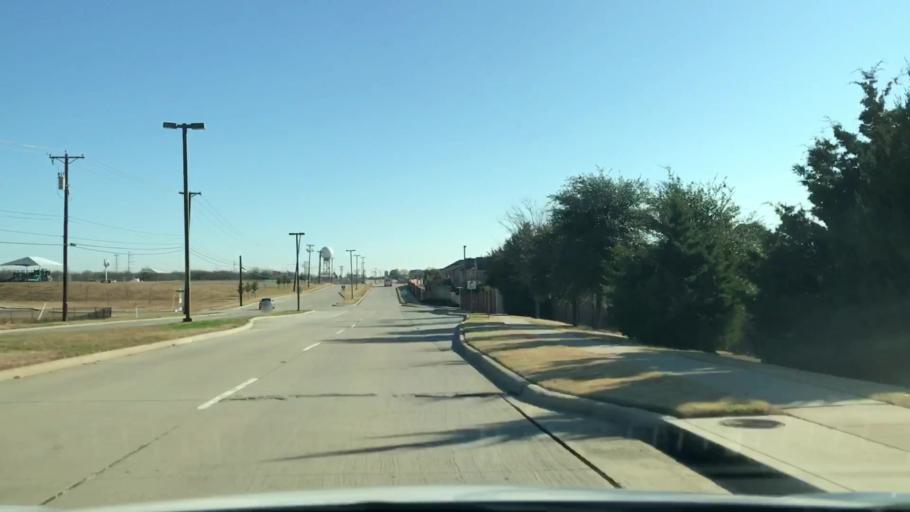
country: US
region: Texas
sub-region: Dallas County
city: Coppell
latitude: 32.9255
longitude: -96.9768
